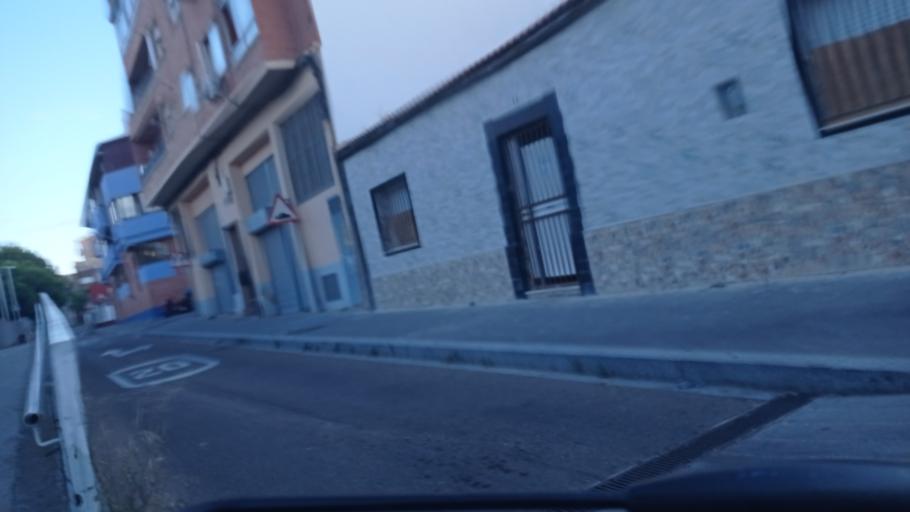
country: ES
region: Aragon
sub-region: Provincia de Zaragoza
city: Oliver-Valdefierro, Oliver, Valdefierro
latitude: 41.6543
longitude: -0.9247
